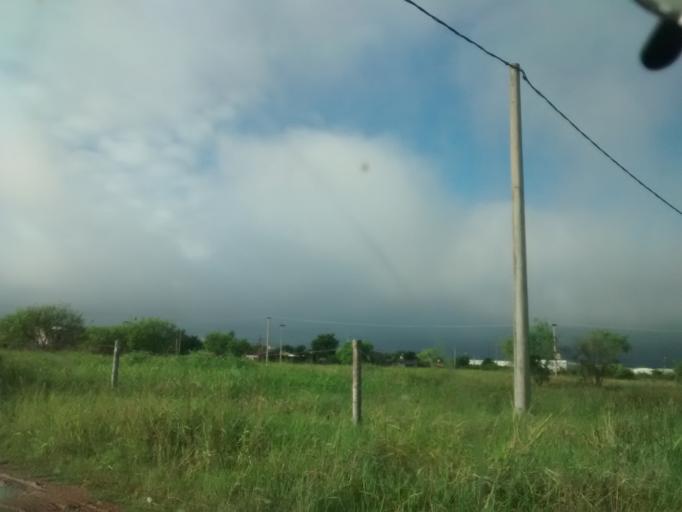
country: AR
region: Chaco
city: Fontana
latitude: -27.4507
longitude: -59.0262
